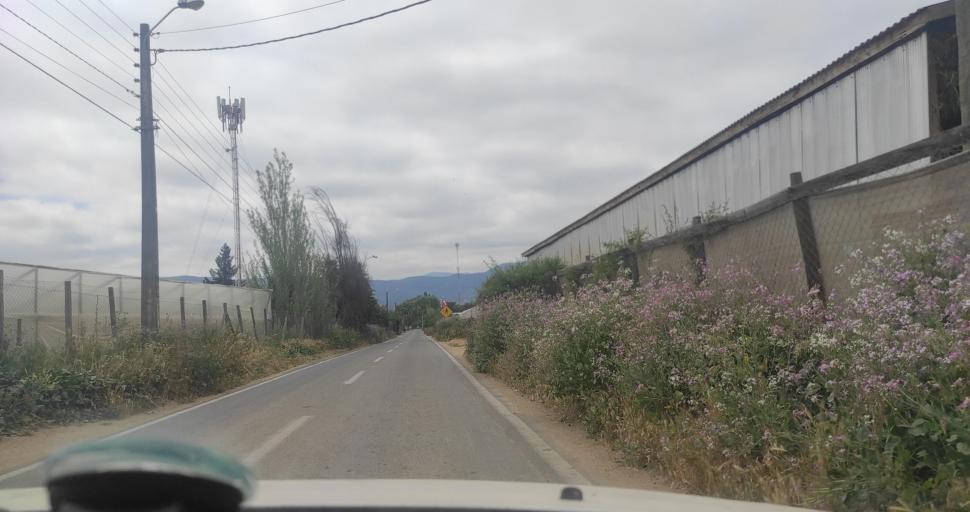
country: CL
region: Valparaiso
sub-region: Provincia de Marga Marga
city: Limache
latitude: -33.0330
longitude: -71.2408
